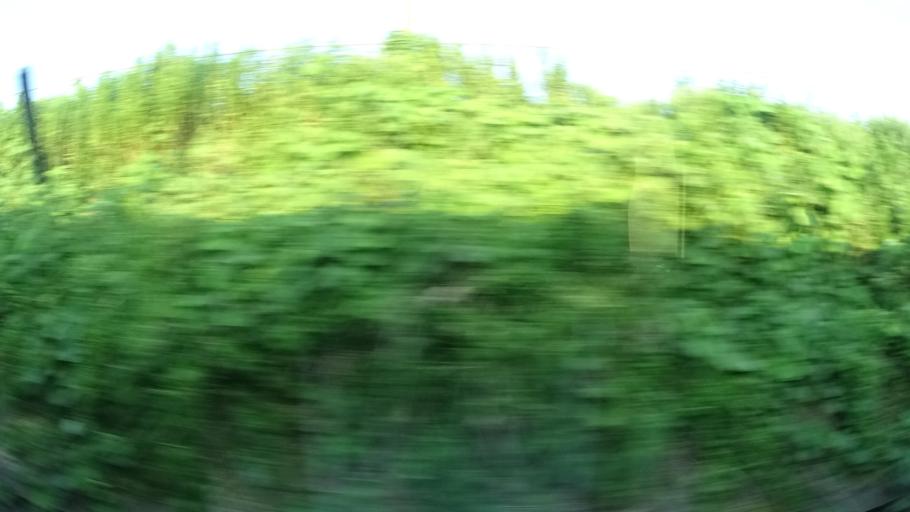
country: JP
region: Ibaraki
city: Tomobe
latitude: 36.3381
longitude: 140.2975
